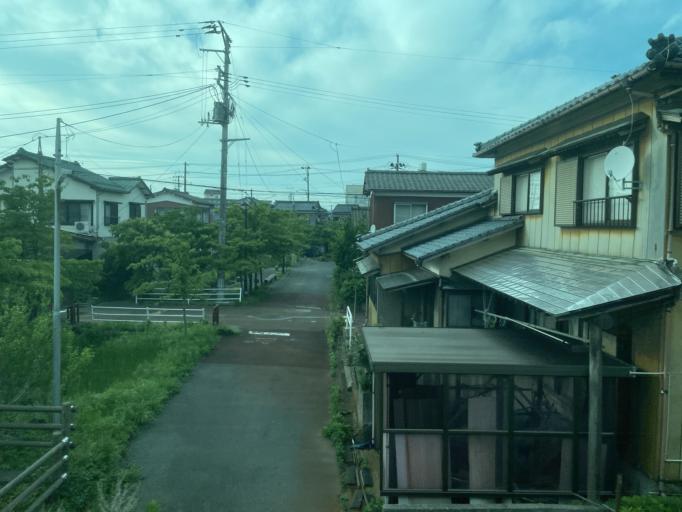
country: JP
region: Niigata
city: Niitsu-honcho
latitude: 37.7932
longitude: 139.1302
